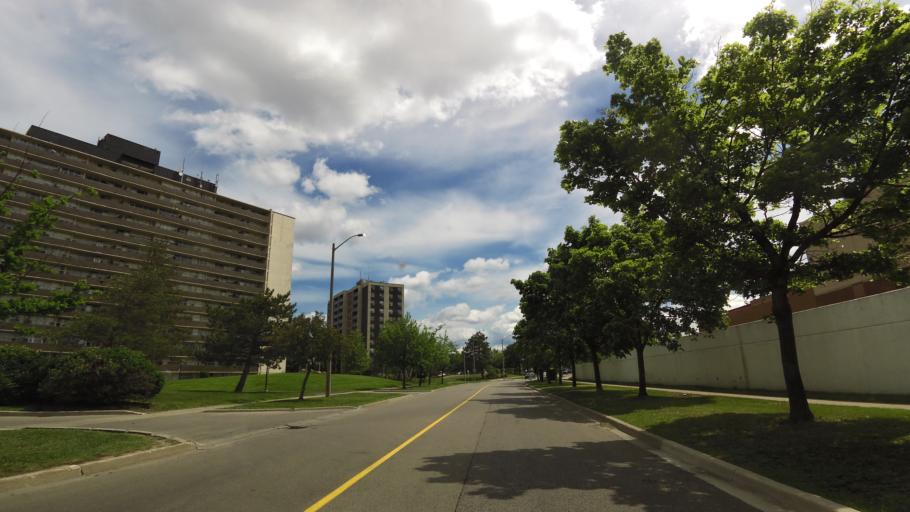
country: CA
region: Ontario
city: Mississauga
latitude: 43.5296
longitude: -79.6514
